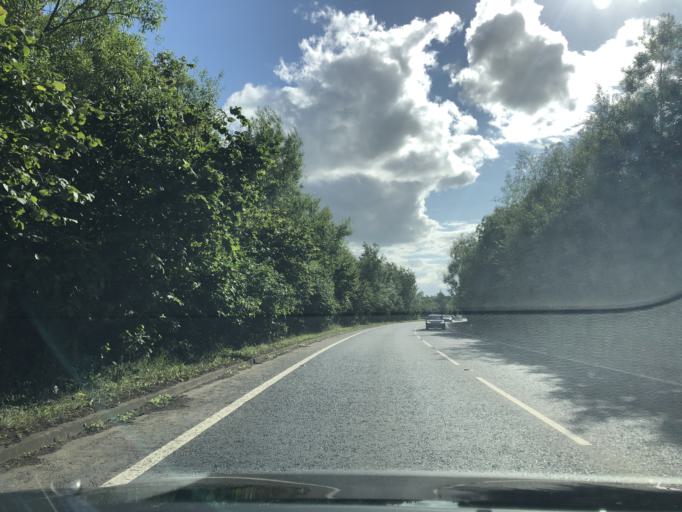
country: GB
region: Northern Ireland
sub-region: Ards District
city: Comber
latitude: 54.5487
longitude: -5.7342
